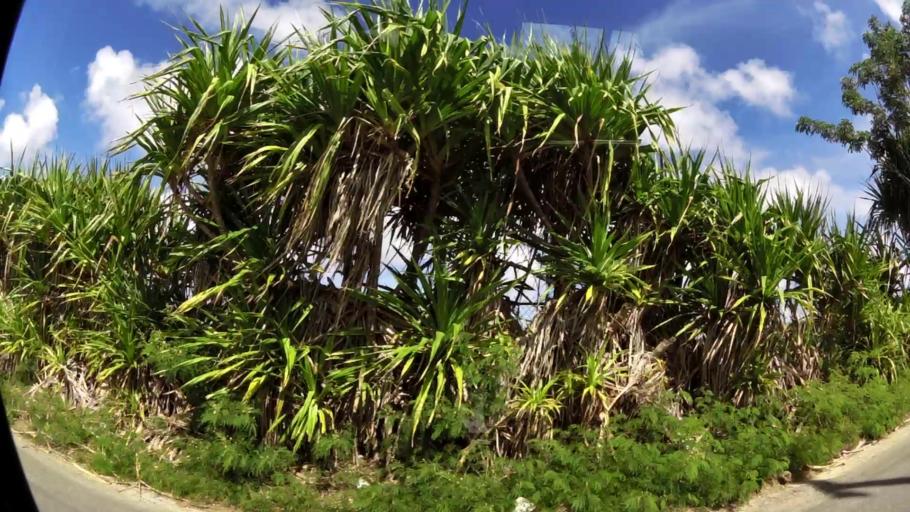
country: BB
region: Saint James
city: Holetown
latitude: 13.2163
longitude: -59.6241
